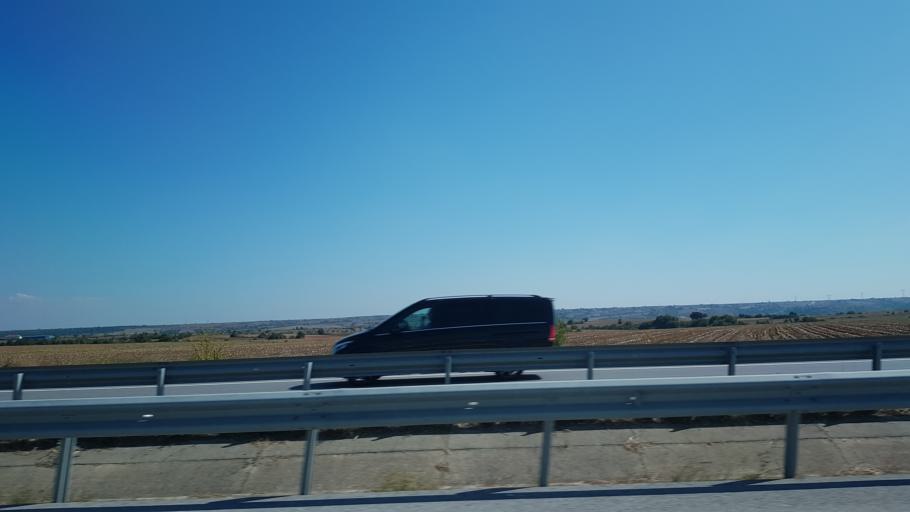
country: TR
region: Kirklareli
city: Babaeski
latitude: 41.5568
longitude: 27.1390
